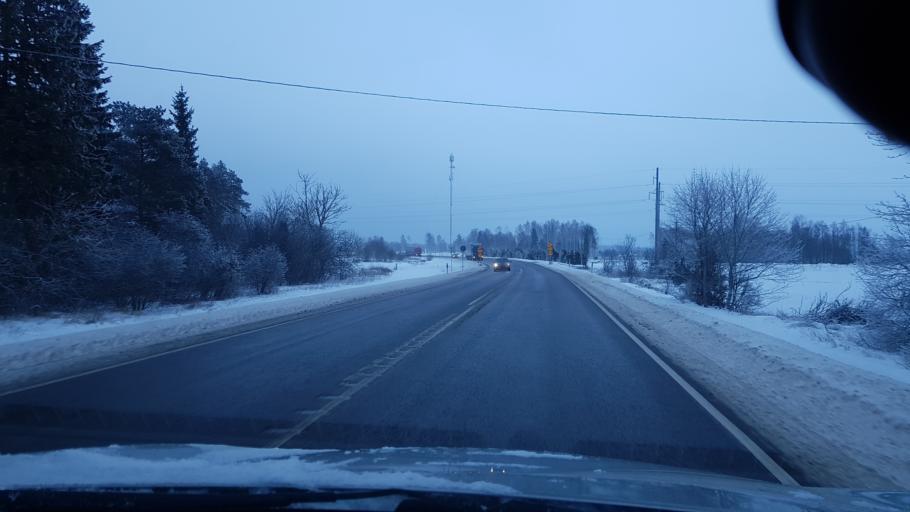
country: EE
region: Harju
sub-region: Keila linn
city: Keila
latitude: 59.3280
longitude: 24.3036
